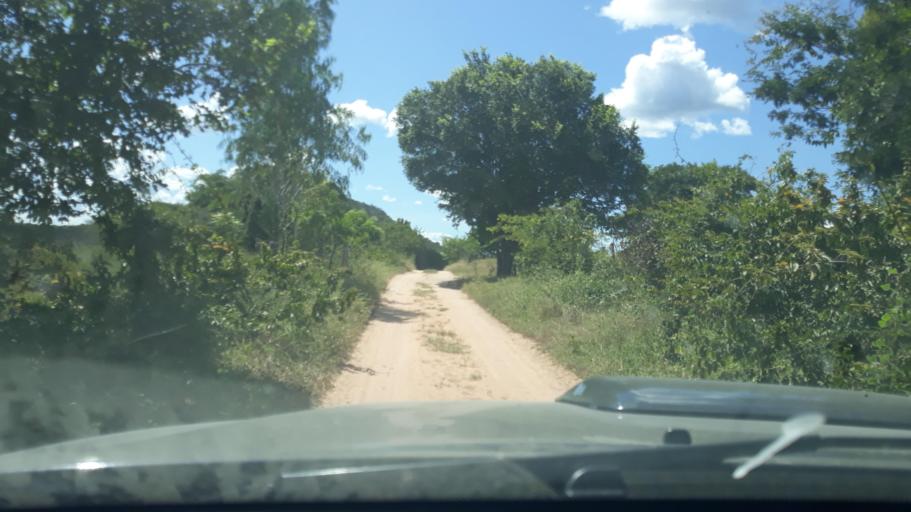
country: BR
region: Bahia
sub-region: Riacho De Santana
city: Riacho de Santana
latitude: -13.8557
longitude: -43.0468
